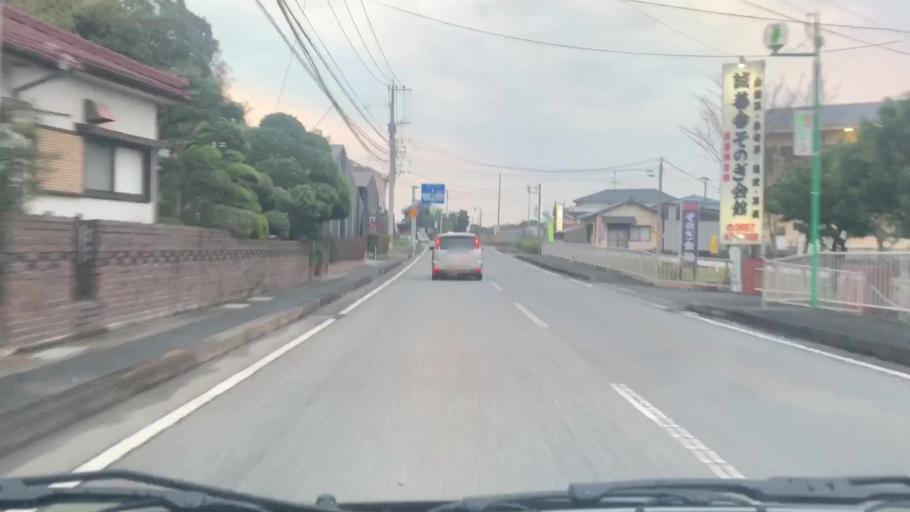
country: JP
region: Saga Prefecture
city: Ureshinomachi-shimojuku
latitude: 33.0389
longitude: 129.9218
